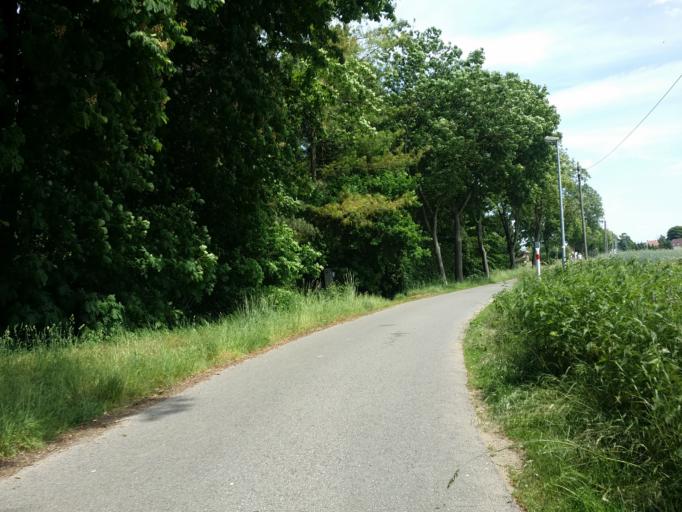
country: DE
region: Lower Saxony
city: Riede
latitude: 52.9781
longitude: 8.8703
